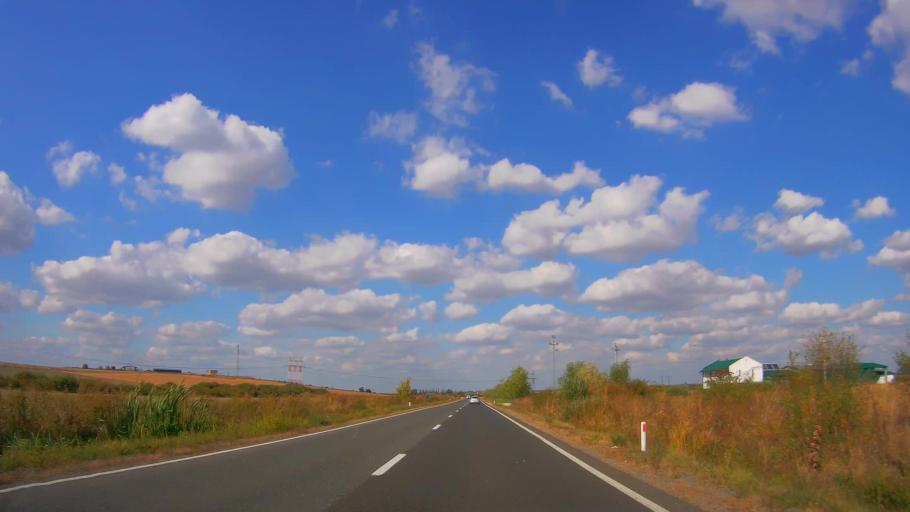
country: RO
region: Satu Mare
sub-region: Oras Ardud
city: Ardud
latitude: 47.6035
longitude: 22.8791
